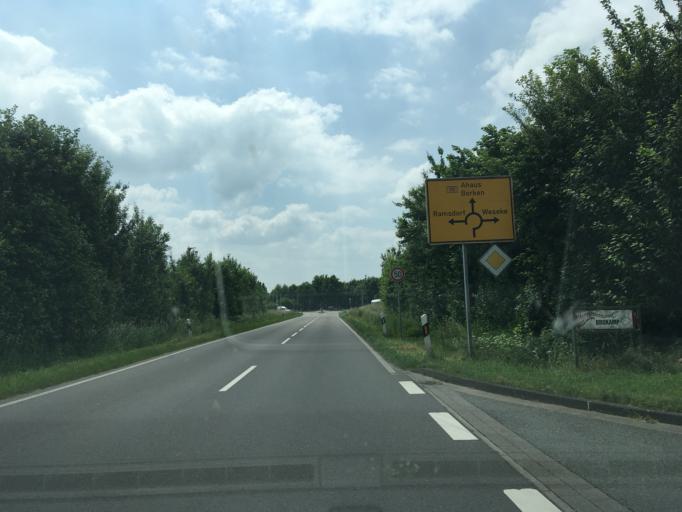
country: DE
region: North Rhine-Westphalia
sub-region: Regierungsbezirk Munster
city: Sudlohn
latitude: 51.9041
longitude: 6.8647
